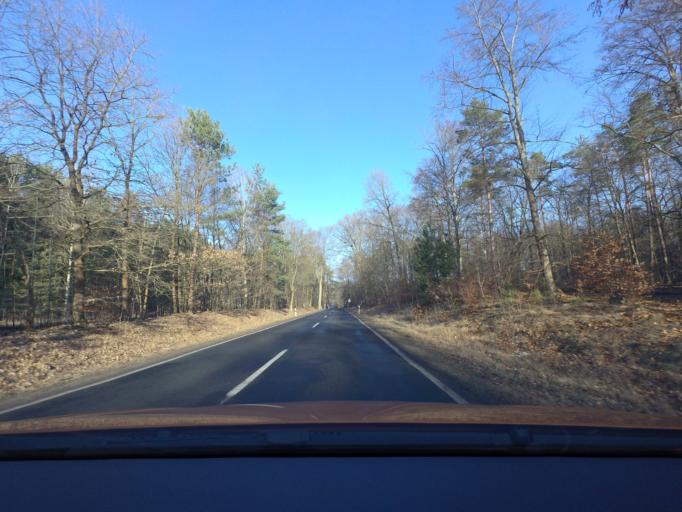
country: DE
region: Brandenburg
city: Wandlitz
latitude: 52.7292
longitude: 13.3681
